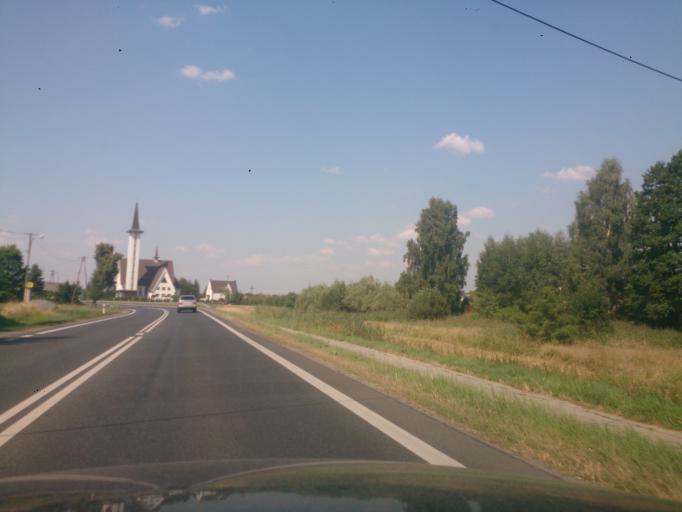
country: PL
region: Subcarpathian Voivodeship
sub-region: Powiat kolbuszowski
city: Kolbuszowa
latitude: 50.2179
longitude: 21.8079
